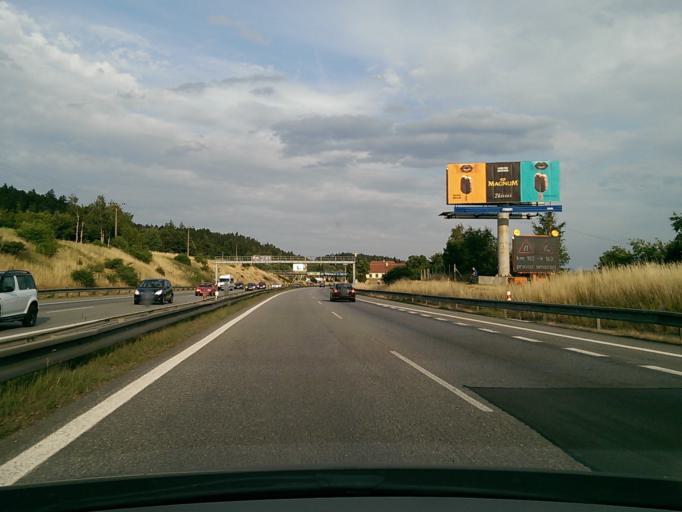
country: CZ
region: Vysocina
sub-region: Okres Zd'ar nad Sazavou
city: Velke Mezirici
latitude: 49.3566
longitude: 16.0253
